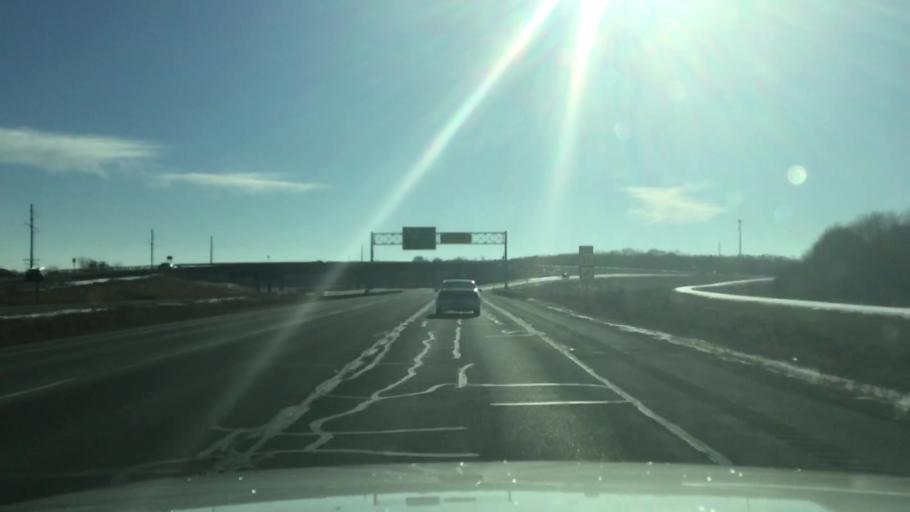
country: US
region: Wisconsin
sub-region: Racine County
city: Rochester
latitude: 42.7195
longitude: -88.2250
